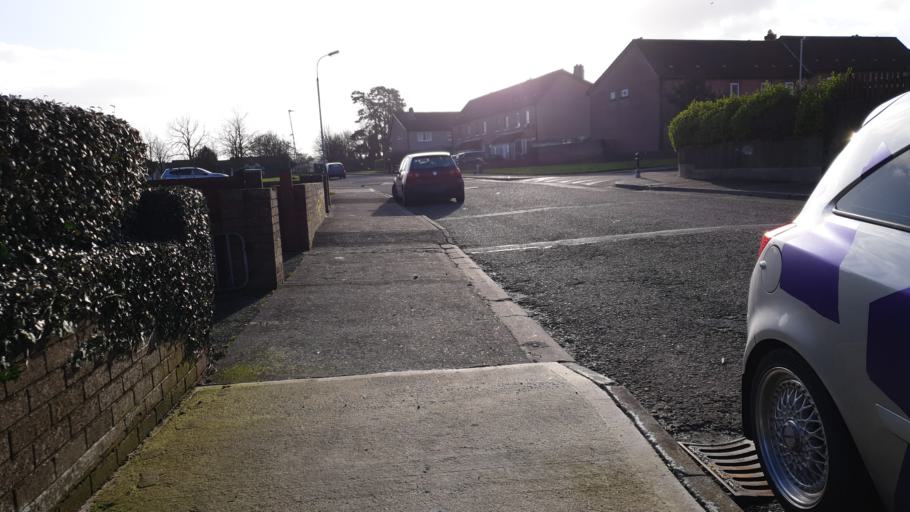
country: IE
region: Munster
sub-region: County Cork
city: Passage West
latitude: 51.8937
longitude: -8.3993
